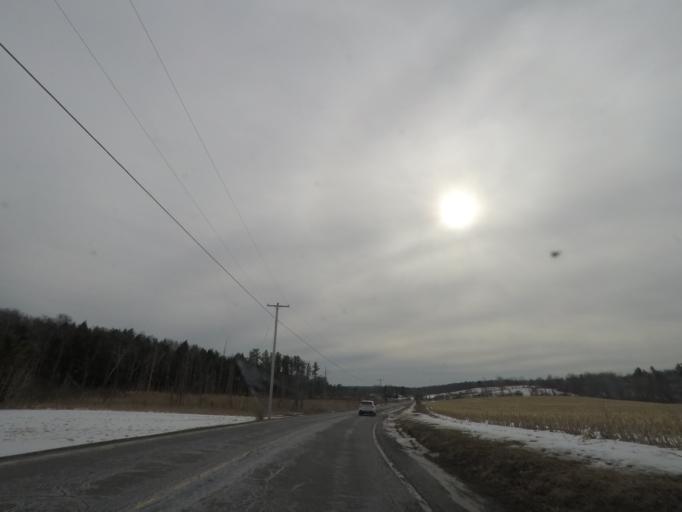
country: US
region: New York
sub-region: Albany County
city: Altamont
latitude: 42.6579
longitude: -74.1333
